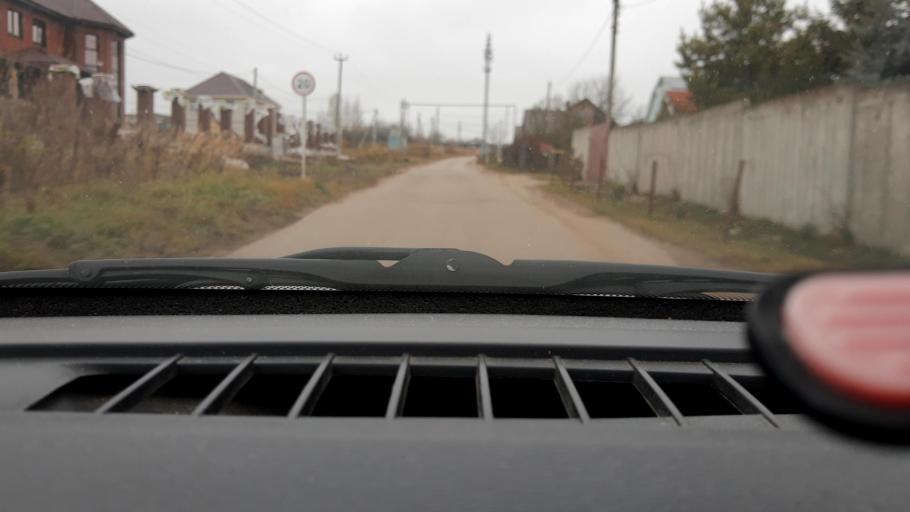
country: RU
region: Nizjnij Novgorod
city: Burevestnik
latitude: 56.1843
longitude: 43.9153
